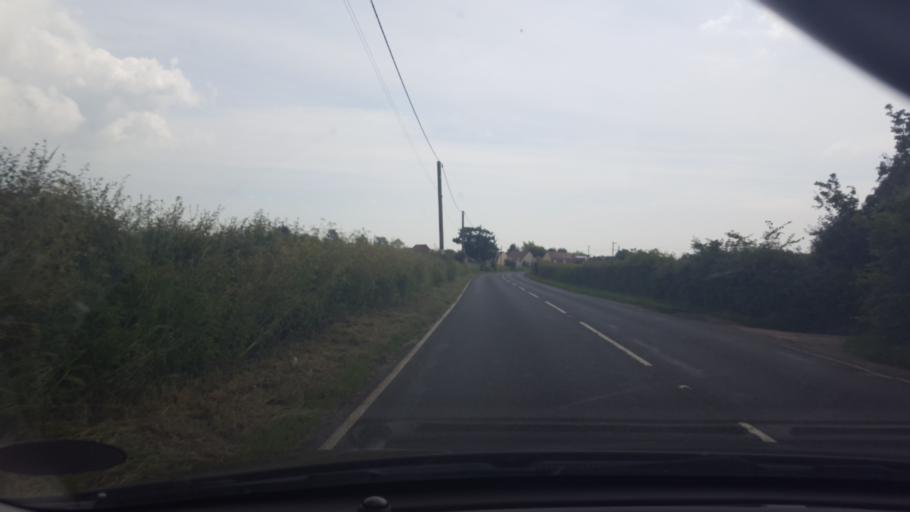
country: GB
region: England
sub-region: Essex
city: Mistley
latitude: 51.8925
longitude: 1.1046
